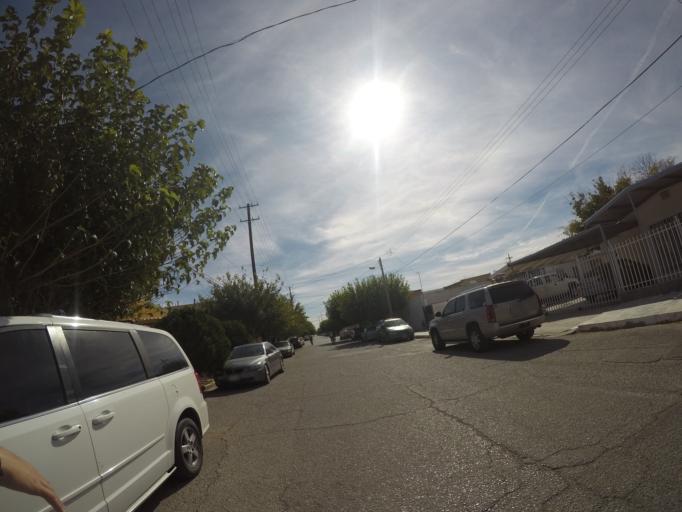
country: MX
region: Chihuahua
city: Ciudad Juarez
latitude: 31.7339
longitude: -106.4360
